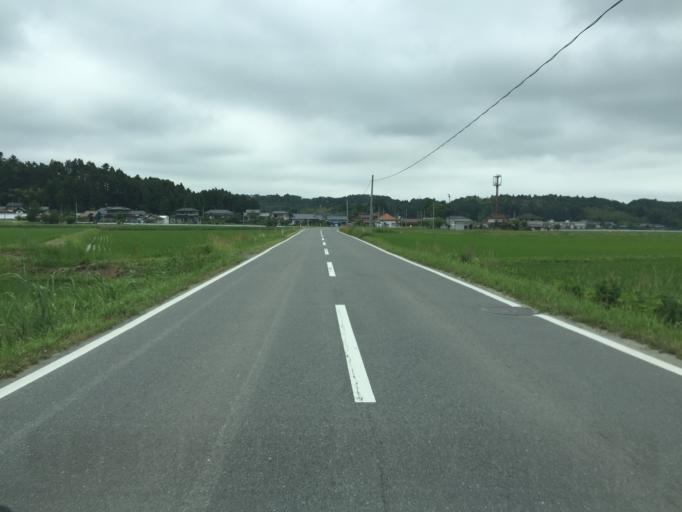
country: JP
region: Miyagi
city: Marumori
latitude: 37.7489
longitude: 140.9154
